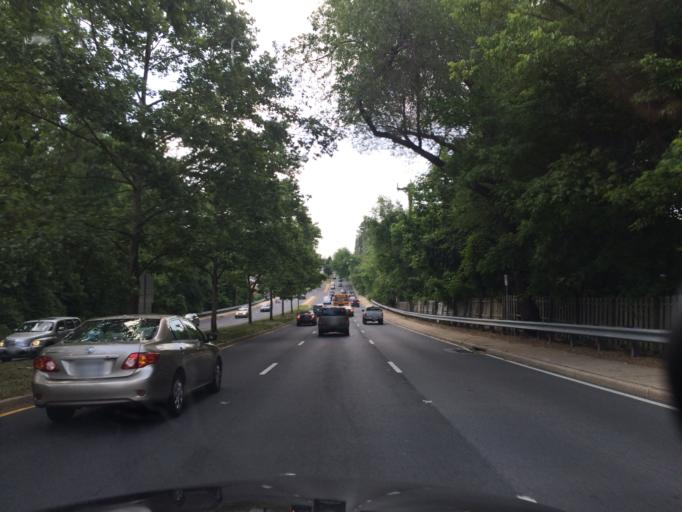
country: US
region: Maryland
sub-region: Montgomery County
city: North Kensington
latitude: 39.0402
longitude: -77.0759
